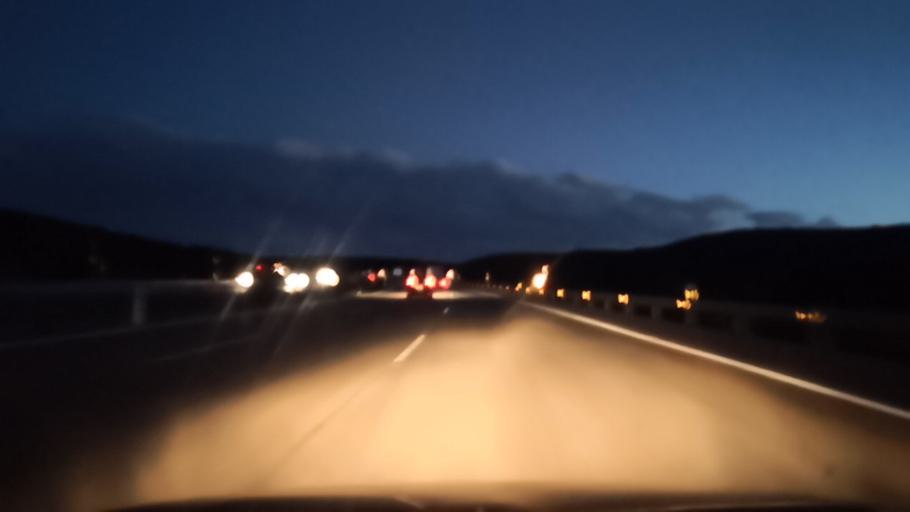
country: ES
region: Castille and Leon
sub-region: Provincia de Leon
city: Villagaton
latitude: 42.5739
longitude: -6.2172
